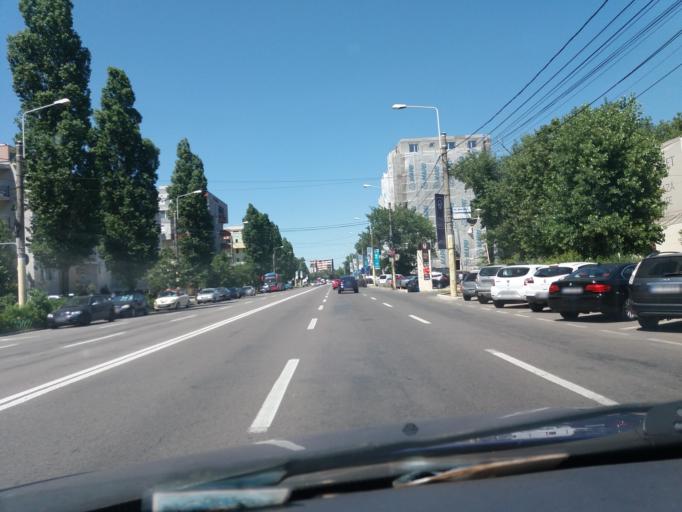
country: RO
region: Constanta
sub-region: Municipiul Constanta
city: Palazu Mare
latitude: 44.2564
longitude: 28.6187
